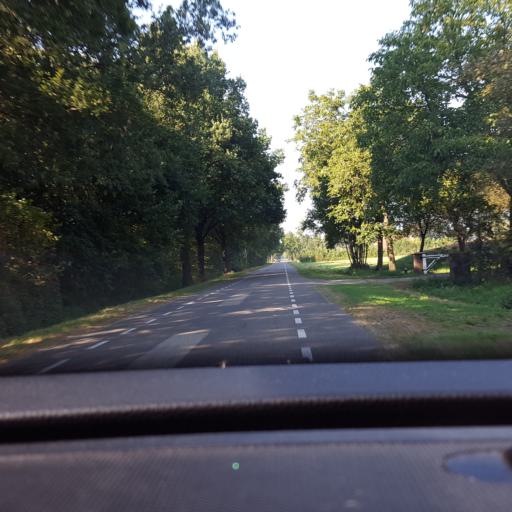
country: NL
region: Gelderland
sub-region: Oude IJsselstreek
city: Varsseveld
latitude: 52.0221
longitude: 6.4577
